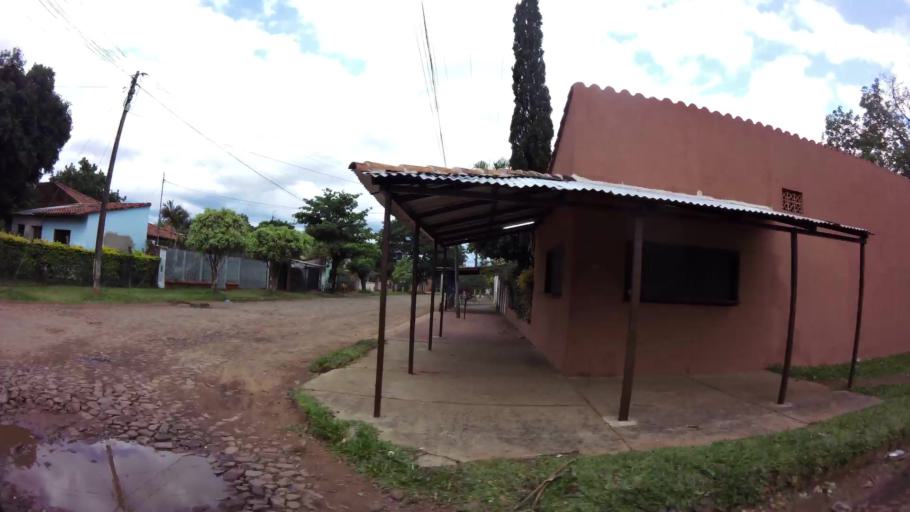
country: PY
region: Central
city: San Lorenzo
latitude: -25.2779
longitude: -57.4884
